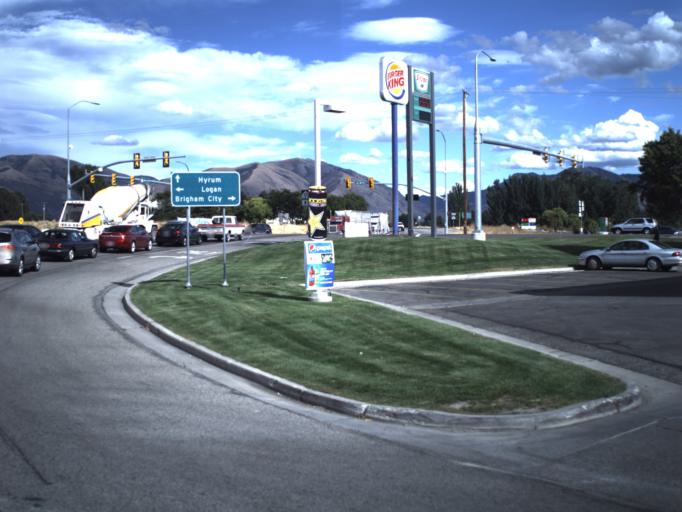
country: US
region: Utah
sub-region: Cache County
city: Wellsville
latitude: 41.6449
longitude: -111.9152
